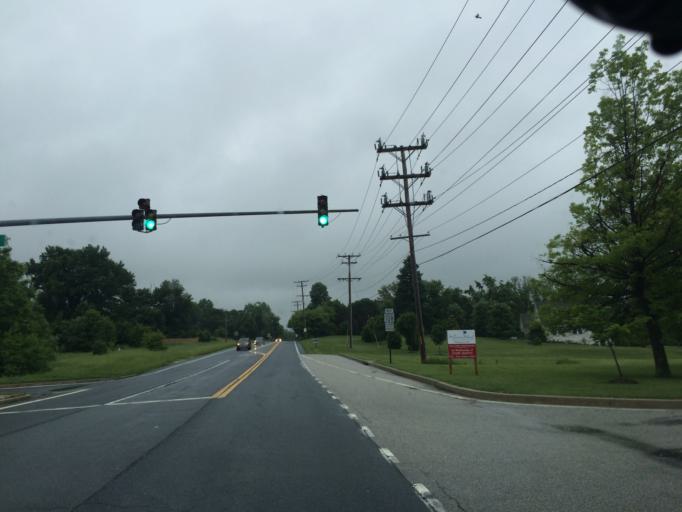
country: US
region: Maryland
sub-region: Howard County
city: Highland
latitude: 39.2040
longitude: -76.9433
